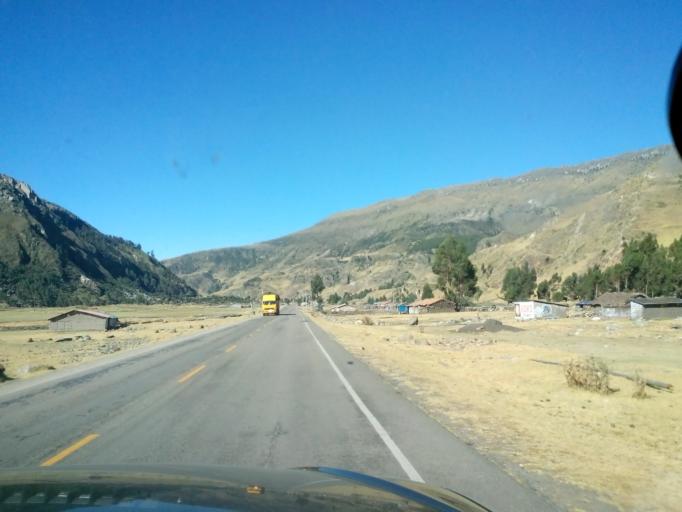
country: PE
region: Ayacucho
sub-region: Provincia de Huamanga
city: Vinchos
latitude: -13.3495
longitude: -74.4749
